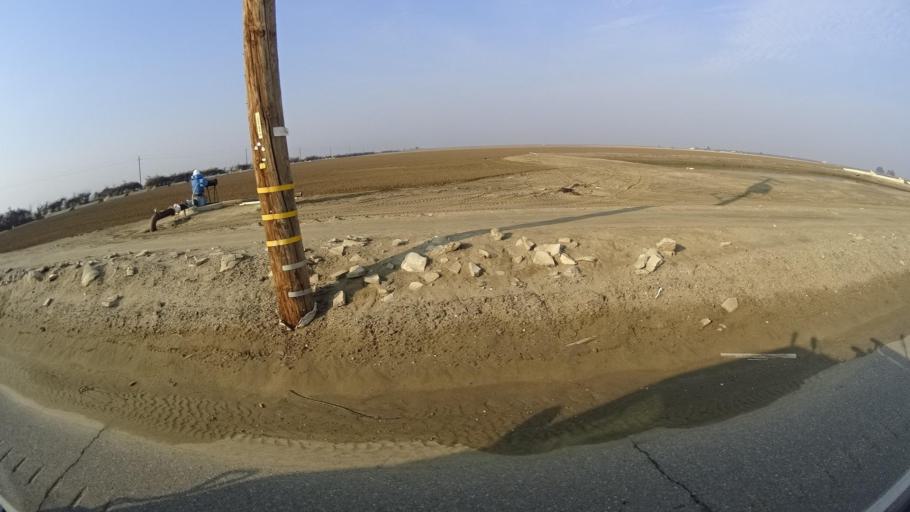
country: US
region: California
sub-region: Kern County
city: Weedpatch
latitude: 35.1376
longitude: -118.9145
